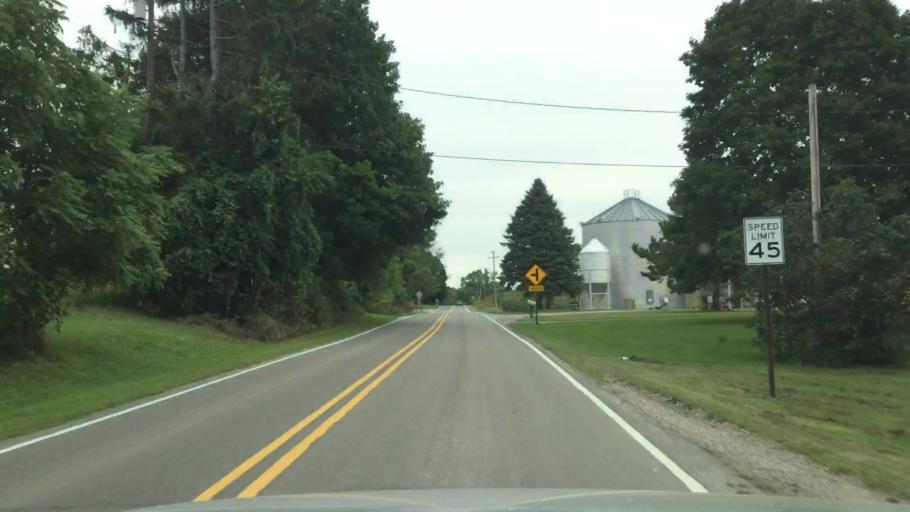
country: US
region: Michigan
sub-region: Washtenaw County
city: Milan
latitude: 42.1487
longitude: -83.6535
